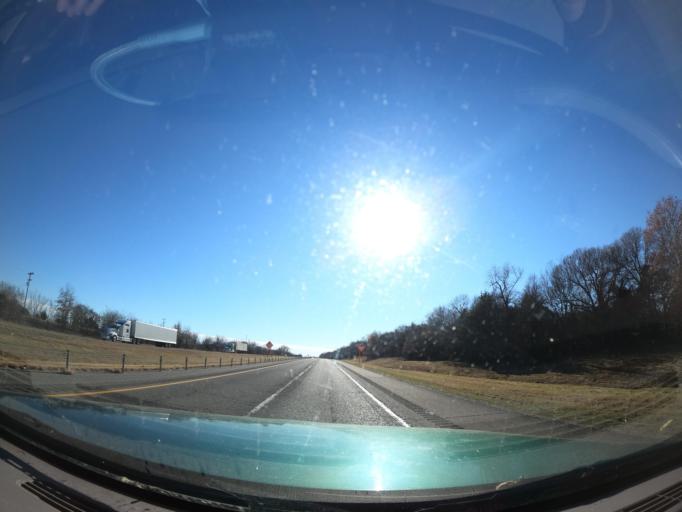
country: US
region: Oklahoma
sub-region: McIntosh County
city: Eufaula
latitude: 35.3743
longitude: -95.5707
